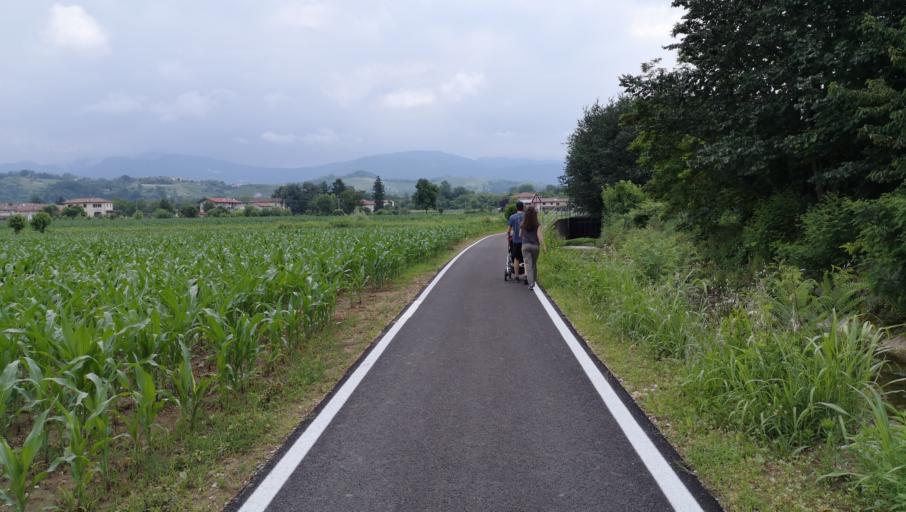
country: IT
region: Friuli Venezia Giulia
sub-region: Provincia di Udine
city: Reana del Rojale
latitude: 46.1615
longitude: 13.2500
